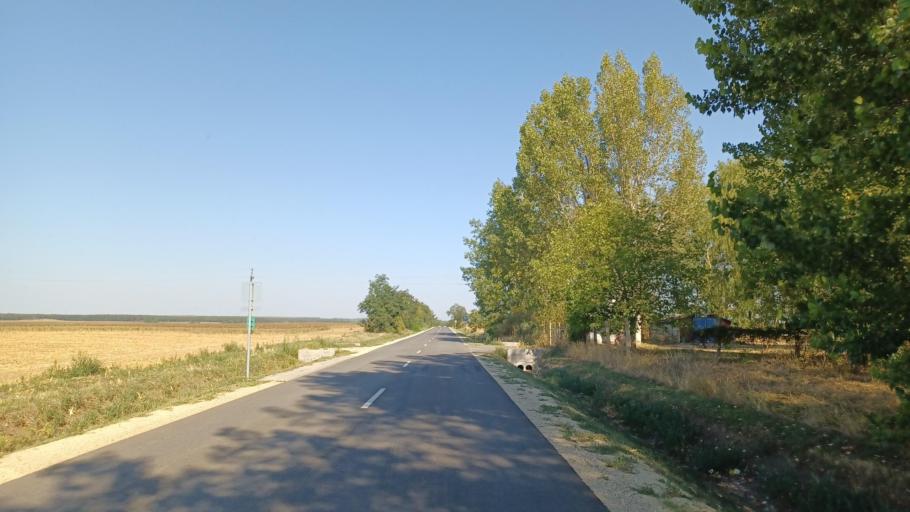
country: HU
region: Tolna
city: Paks
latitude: 46.6565
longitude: 18.8340
